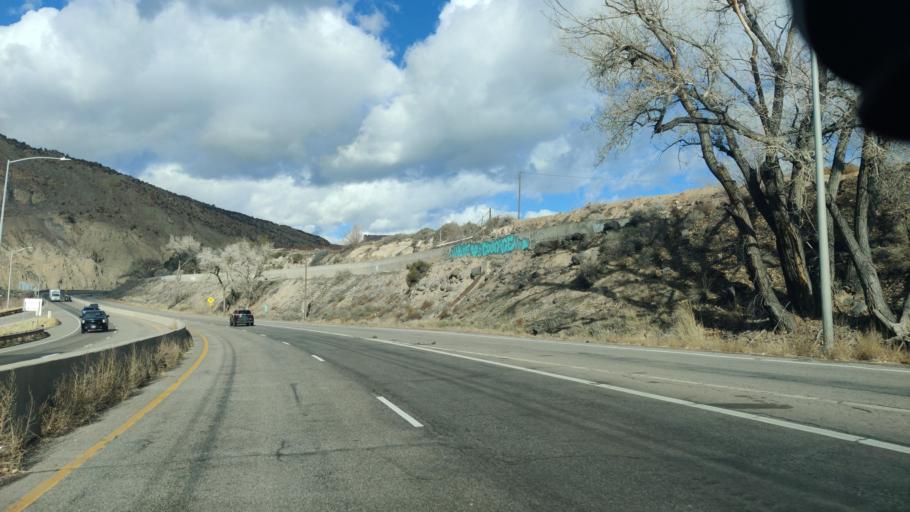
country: US
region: Colorado
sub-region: Mesa County
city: Palisade
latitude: 39.1260
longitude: -108.3222
